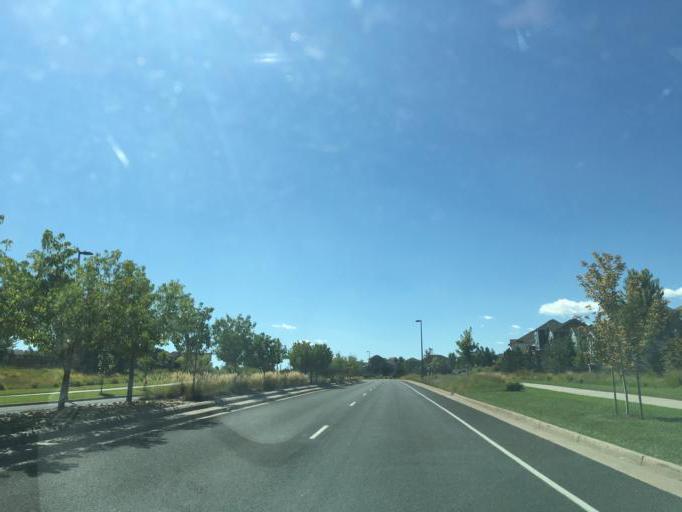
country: US
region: Colorado
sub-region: Douglas County
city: Parker
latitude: 39.6044
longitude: -104.6857
